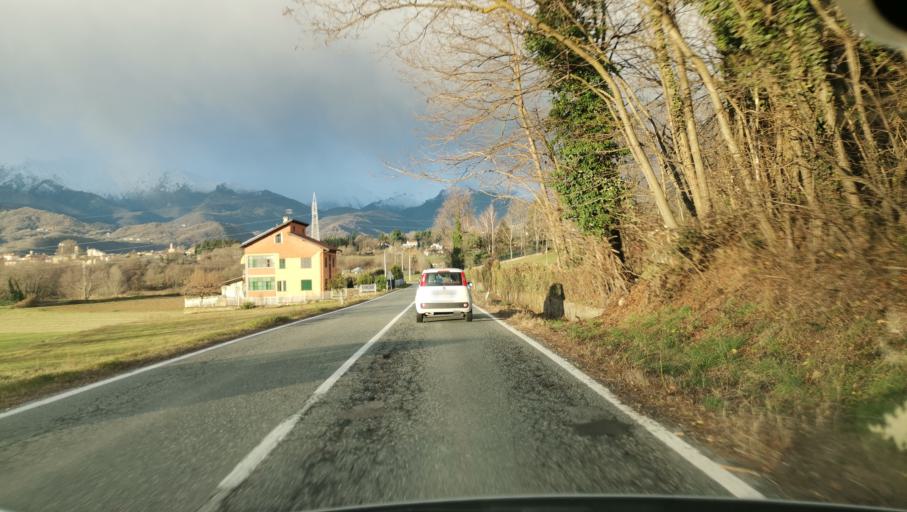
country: IT
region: Piedmont
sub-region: Provincia di Torino
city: Giaveno
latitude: 45.0488
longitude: 7.3704
